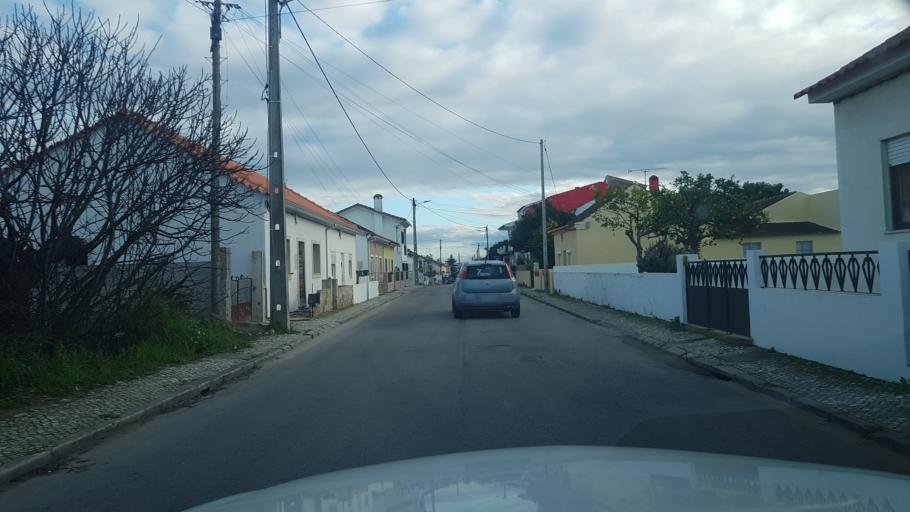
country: PT
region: Santarem
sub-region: Entroncamento
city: Entroncamento
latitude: 39.4760
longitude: -8.4805
